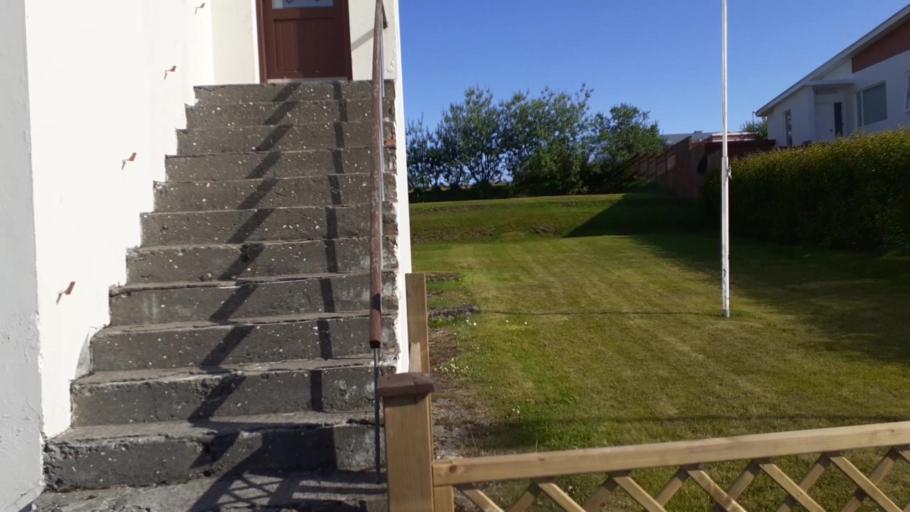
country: IS
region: Northeast
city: Dalvik
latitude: 65.9785
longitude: -18.3739
